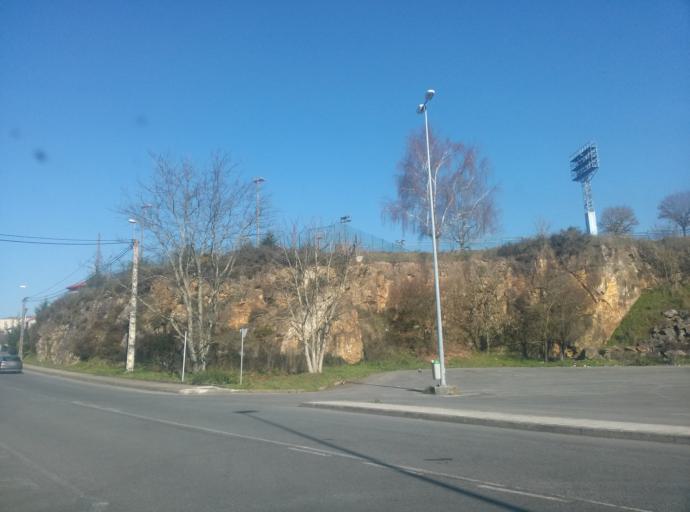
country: ES
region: Galicia
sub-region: Provincia de Lugo
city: Lugo
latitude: 43.0028
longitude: -7.5729
